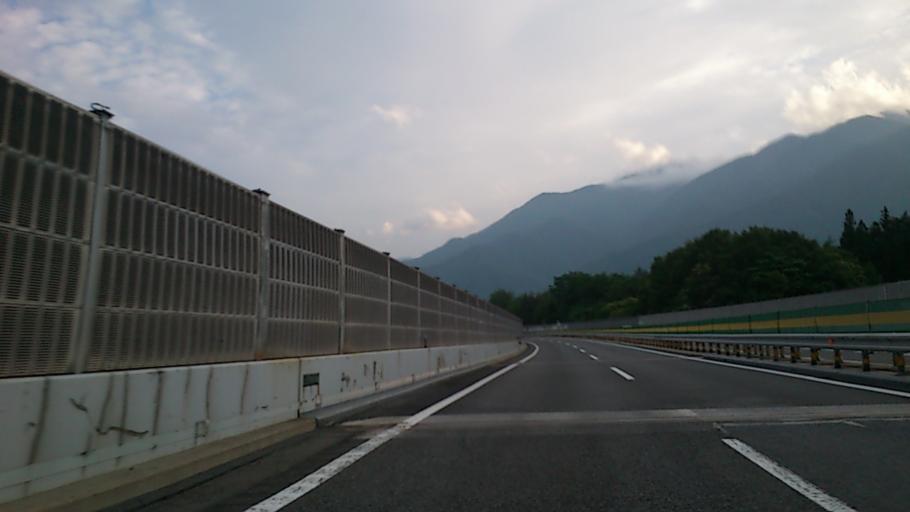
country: JP
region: Nagano
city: Ina
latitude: 35.7548
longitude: 137.9151
